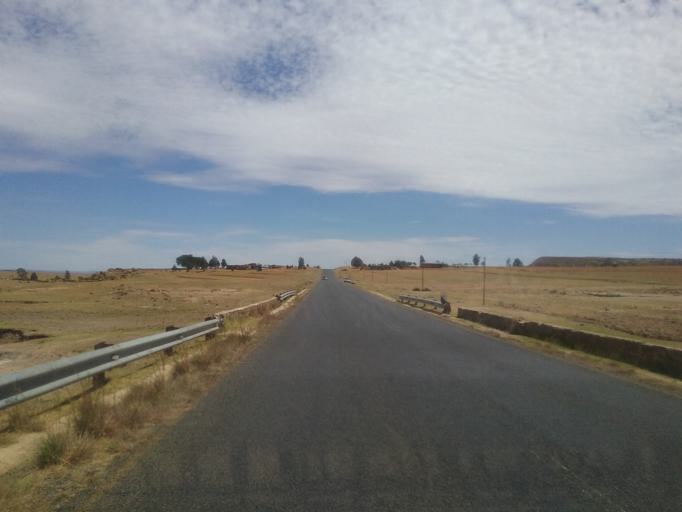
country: LS
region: Mafeteng
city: Mafeteng
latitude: -29.8866
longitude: 27.2495
